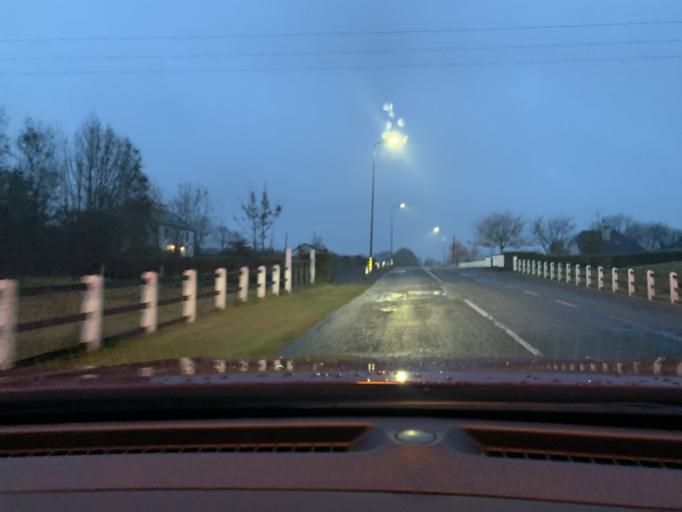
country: IE
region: Connaught
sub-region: Sligo
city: Ballymote
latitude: 53.9981
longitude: -8.5215
